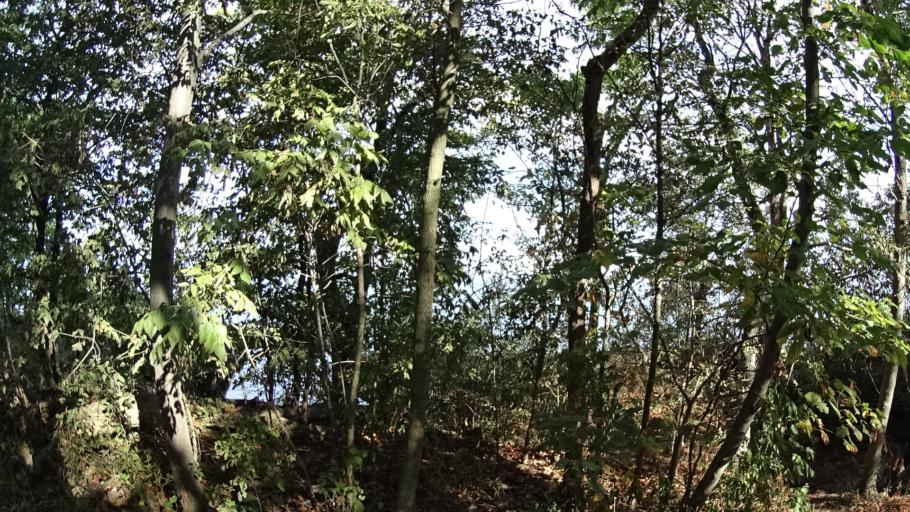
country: US
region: Ohio
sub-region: Erie County
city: Sandusky
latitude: 41.6168
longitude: -82.6827
